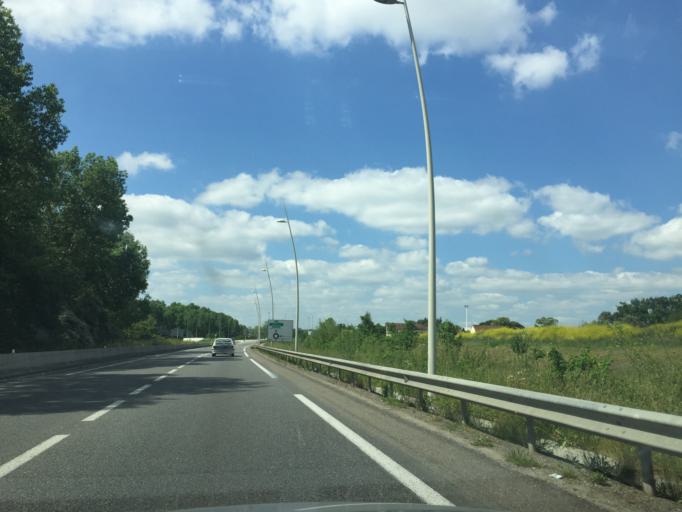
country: FR
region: Aquitaine
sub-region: Departement du Lot-et-Garonne
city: Boe
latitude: 44.1764
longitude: 0.6170
